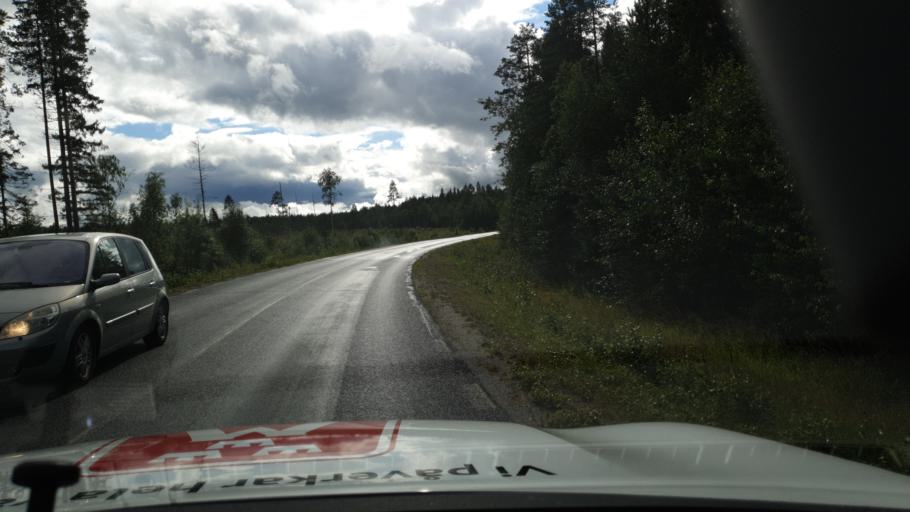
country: SE
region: Vaesterbotten
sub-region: Skelleftea Kommun
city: Soedra Bergsbyn
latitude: 64.5889
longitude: 21.0393
